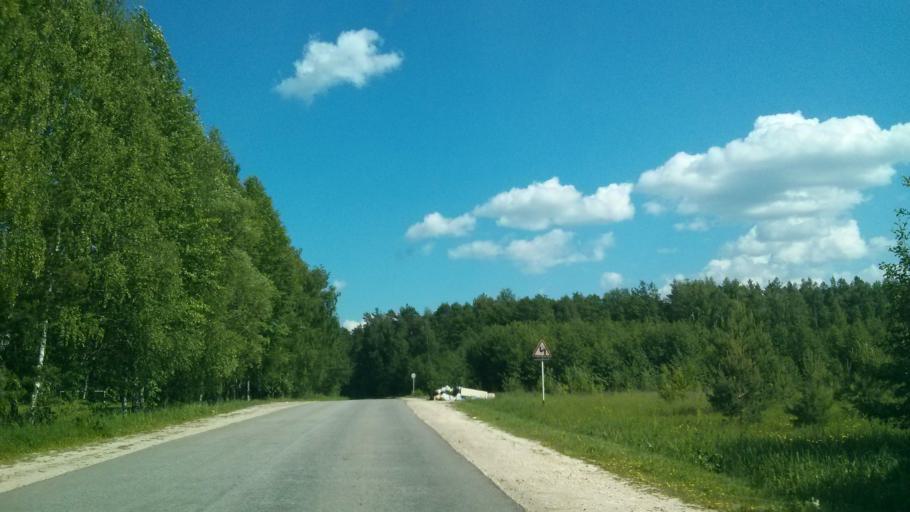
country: RU
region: Vladimir
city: Melenki
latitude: 55.3342
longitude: 41.6683
